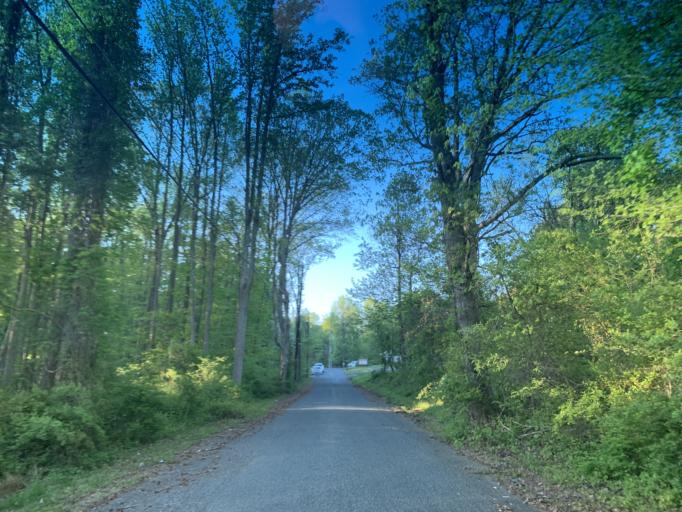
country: US
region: Maryland
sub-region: Harford County
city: Aberdeen
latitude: 39.5166
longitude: -76.1932
